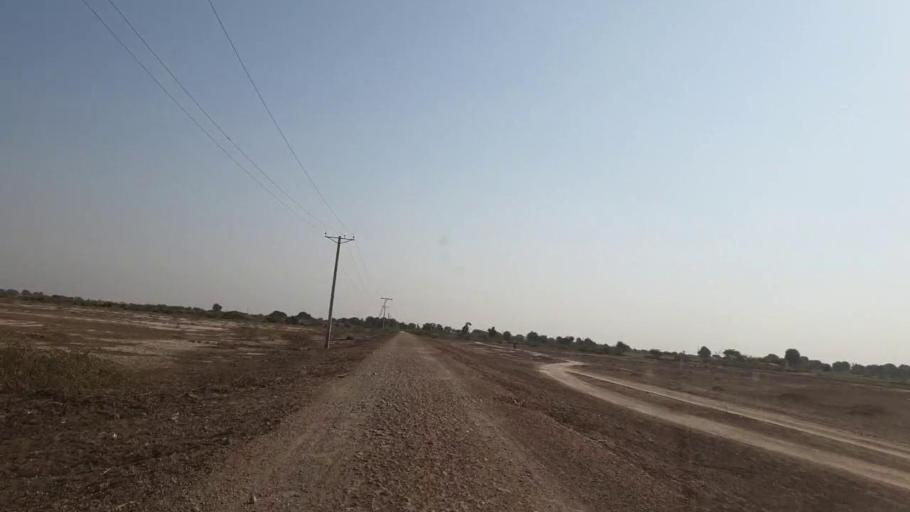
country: PK
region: Sindh
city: Naukot
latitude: 25.0152
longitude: 69.4746
